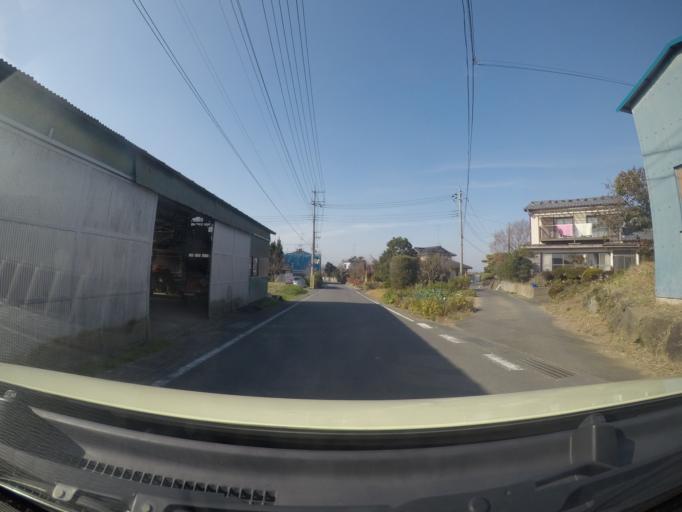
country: JP
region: Ibaraki
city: Tsukuba
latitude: 36.2154
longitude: 140.0716
